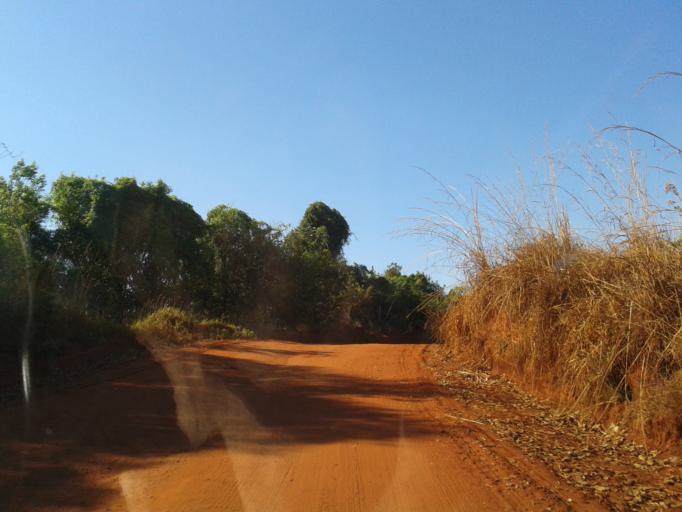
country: BR
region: Minas Gerais
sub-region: Ituiutaba
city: Ituiutaba
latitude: -18.9992
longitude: -49.3703
